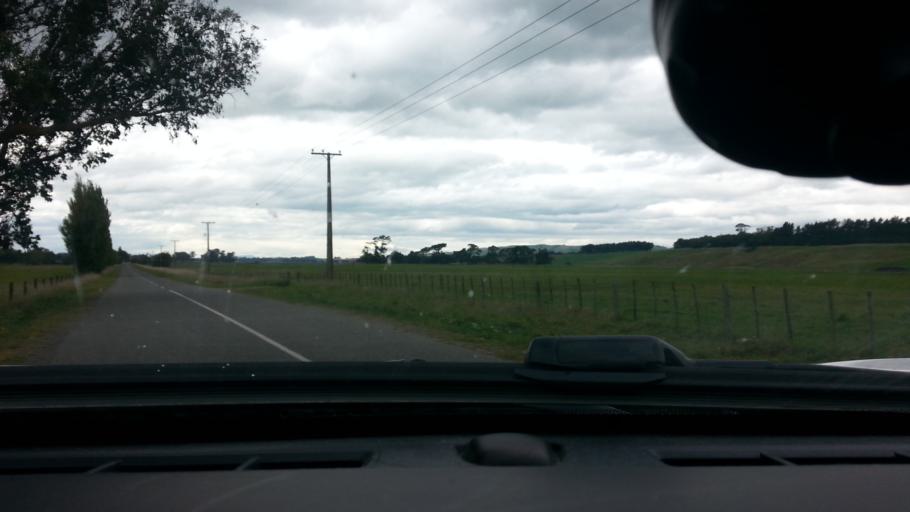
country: NZ
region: Wellington
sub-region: South Wairarapa District
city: Waipawa
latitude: -41.1704
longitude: 175.4204
